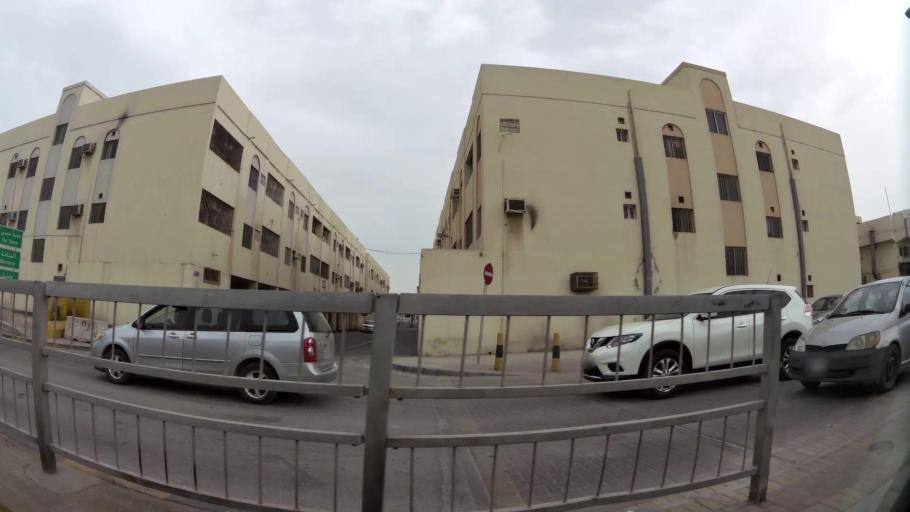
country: BH
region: Manama
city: Jidd Hafs
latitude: 26.2071
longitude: 50.5500
